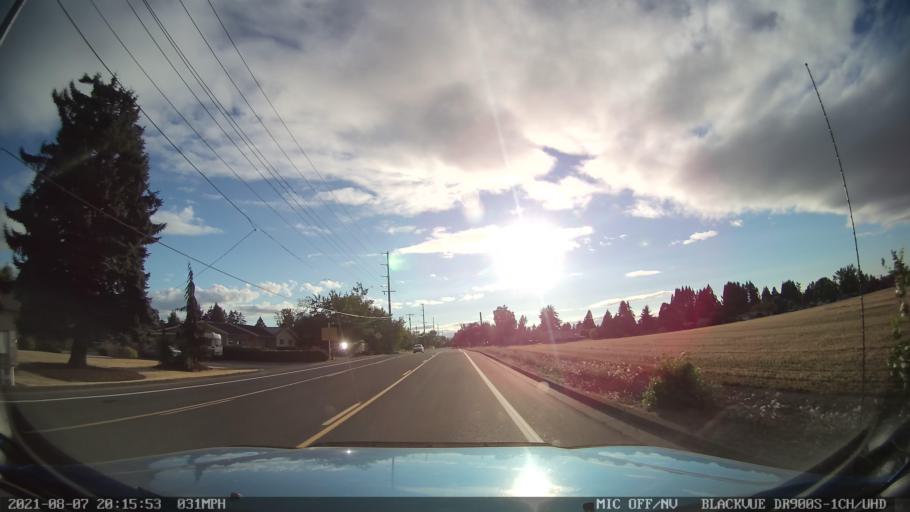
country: US
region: Oregon
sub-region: Marion County
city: Four Corners
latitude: 44.9549
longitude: -122.9599
